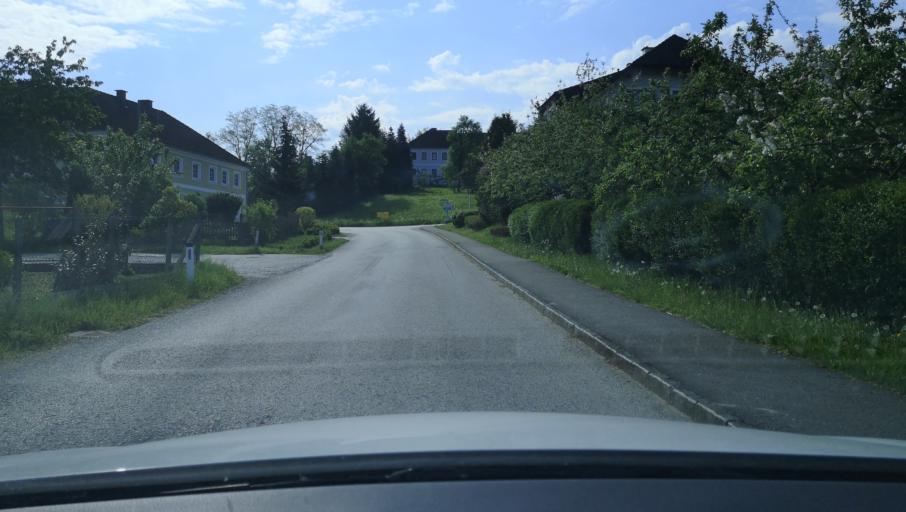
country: AT
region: Lower Austria
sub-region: Politischer Bezirk Amstetten
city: Neuhofen an der Ybbs
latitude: 48.0584
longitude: 14.8621
